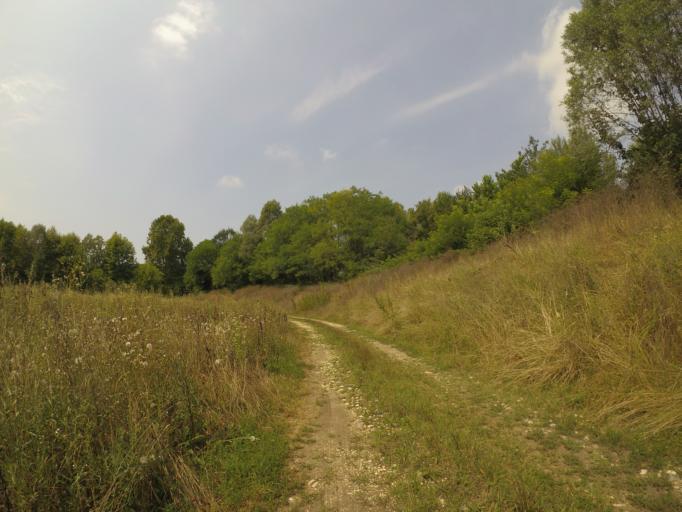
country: IT
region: Friuli Venezia Giulia
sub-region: Provincia di Udine
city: Varmo
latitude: 45.9046
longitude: 13.0208
